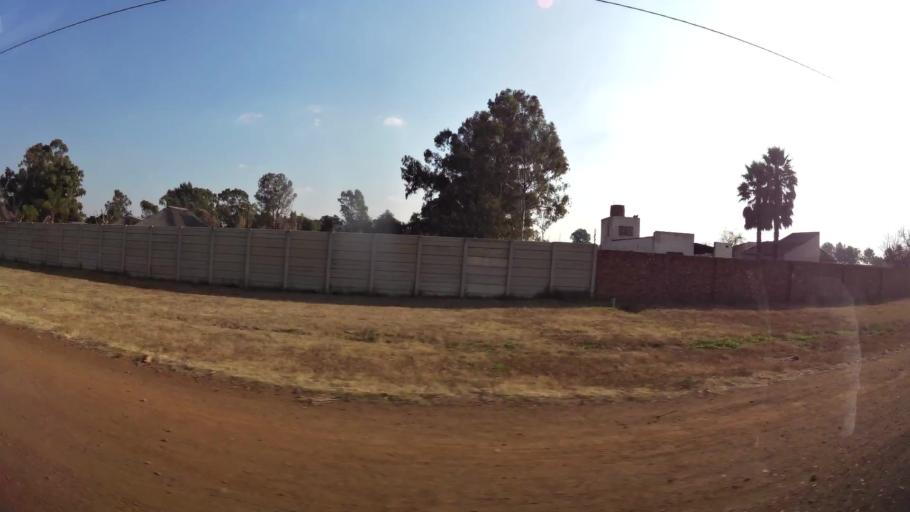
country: ZA
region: Gauteng
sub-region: Ekurhuleni Metropolitan Municipality
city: Benoni
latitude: -26.1184
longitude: 28.3904
